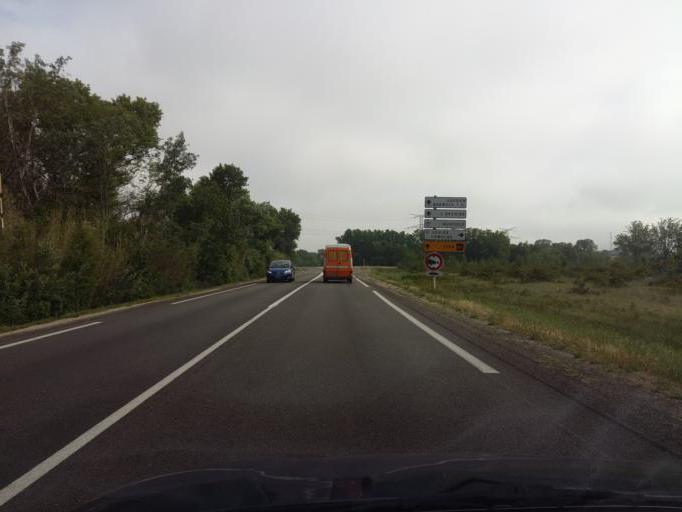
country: FR
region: Languedoc-Roussillon
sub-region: Departement du Gard
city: Saint-Genies-de-Comolas
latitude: 44.0765
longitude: 4.7075
